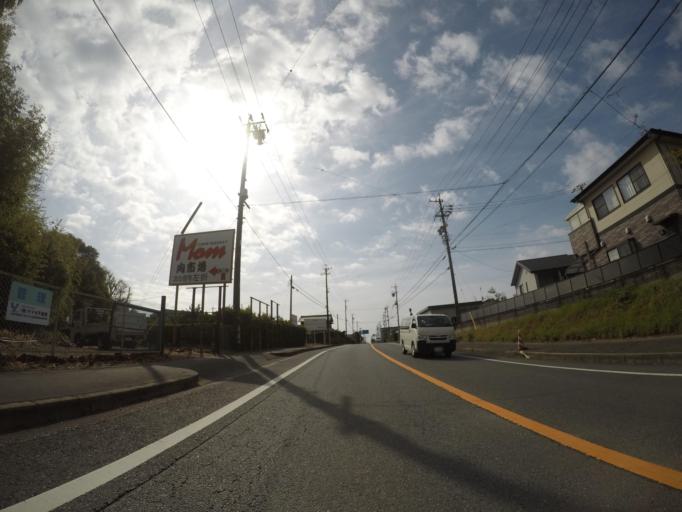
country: JP
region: Shizuoka
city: Hamakita
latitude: 34.8021
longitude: 137.6969
